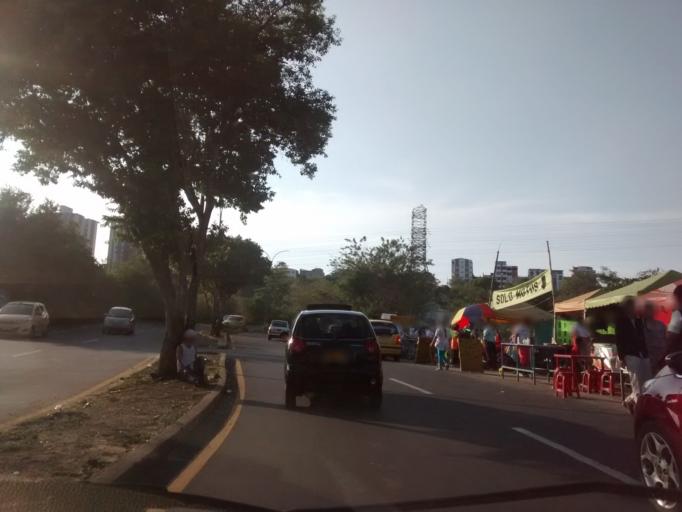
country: CO
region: Santander
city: Bucaramanga
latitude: 7.0920
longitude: -73.1299
